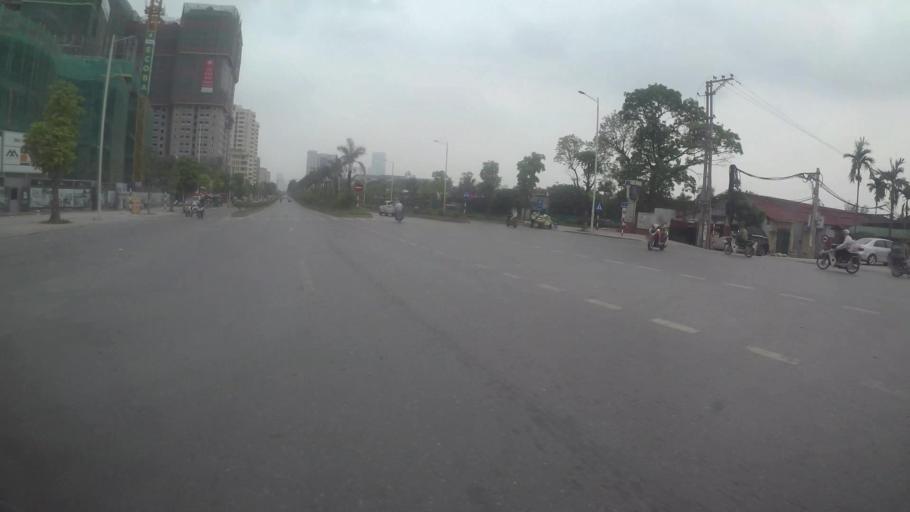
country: VN
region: Ha Noi
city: Cau Dien
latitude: 21.0308
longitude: 105.7591
